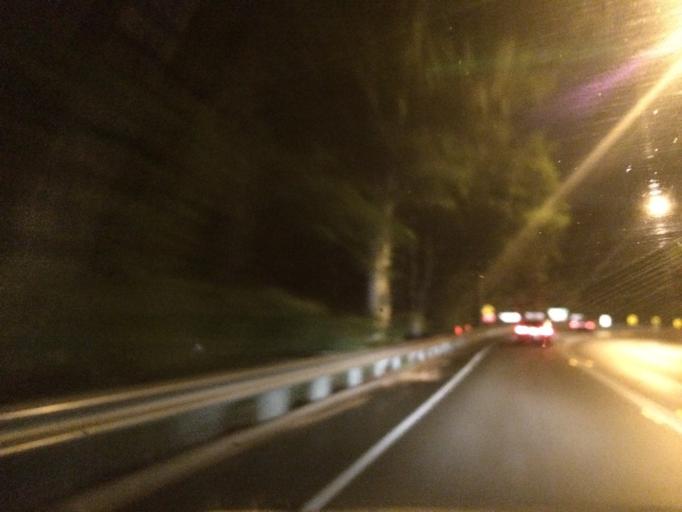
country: AU
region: Queensland
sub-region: Brisbane
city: Kenmore Hills
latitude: -27.5136
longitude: 152.9333
